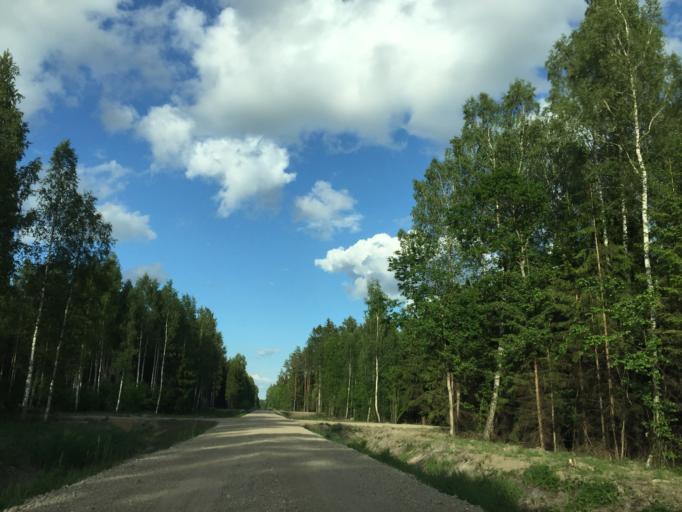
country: LV
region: Engure
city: Smarde
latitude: 56.7765
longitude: 23.3988
